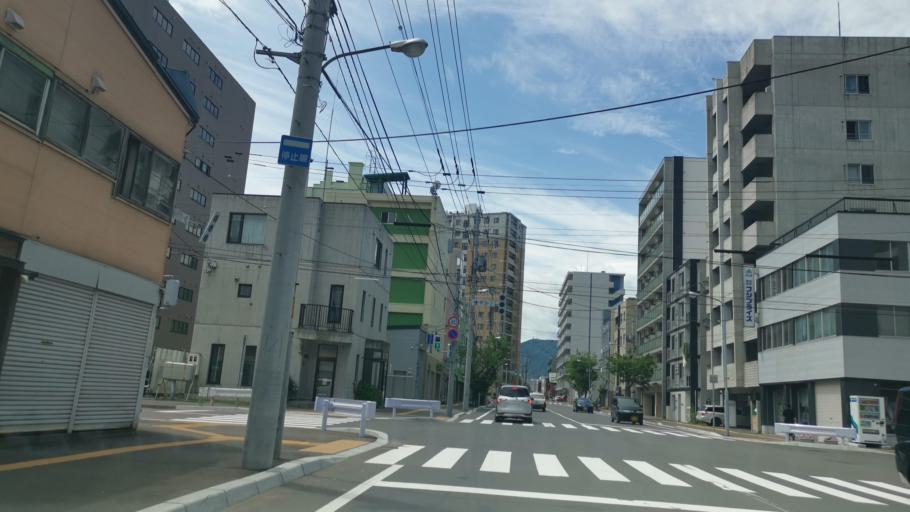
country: JP
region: Hokkaido
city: Sapporo
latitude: 43.0553
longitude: 141.3681
